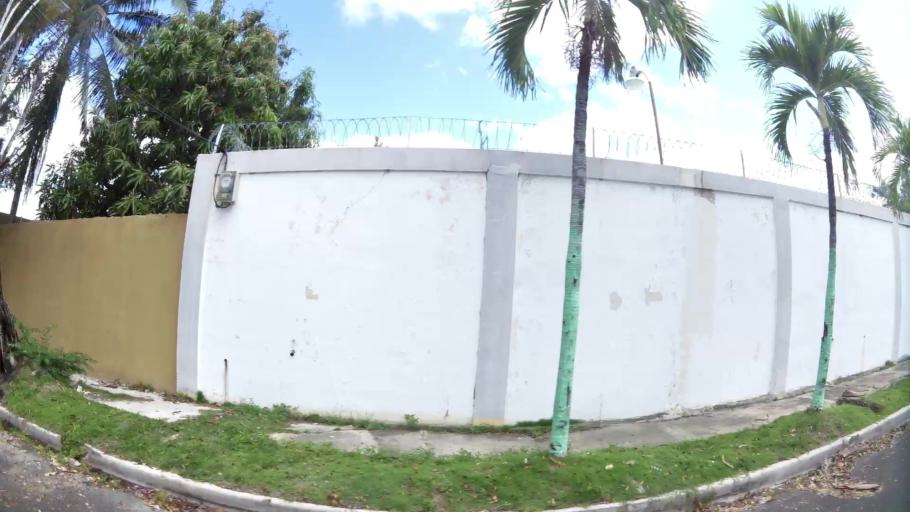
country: DO
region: Nacional
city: Ensanche Luperon
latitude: 18.5167
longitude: -69.9078
